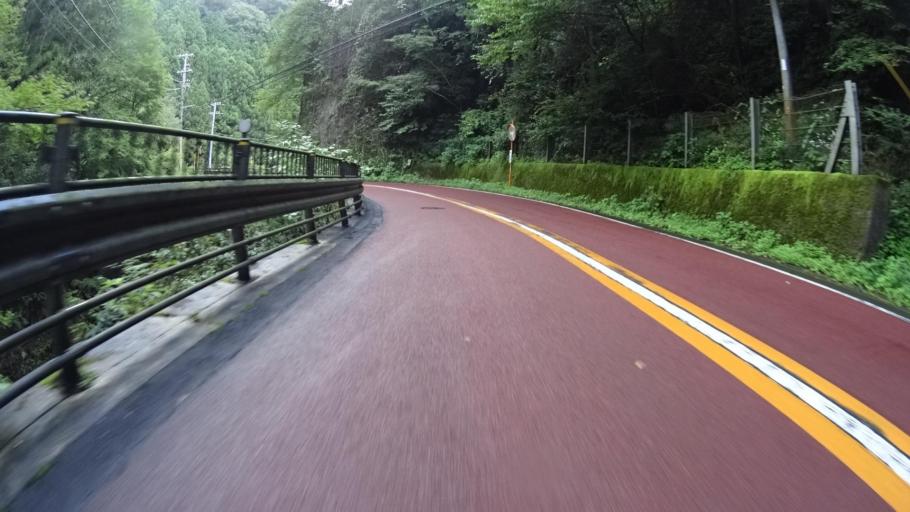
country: JP
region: Tokyo
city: Itsukaichi
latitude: 35.7417
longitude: 139.1228
